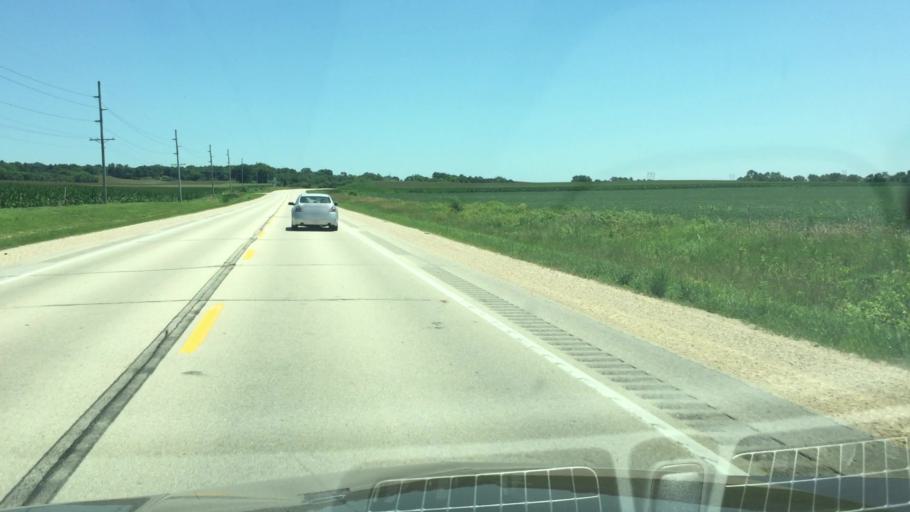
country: US
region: Iowa
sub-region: Jackson County
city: Maquoketa
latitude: 42.0655
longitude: -90.7715
